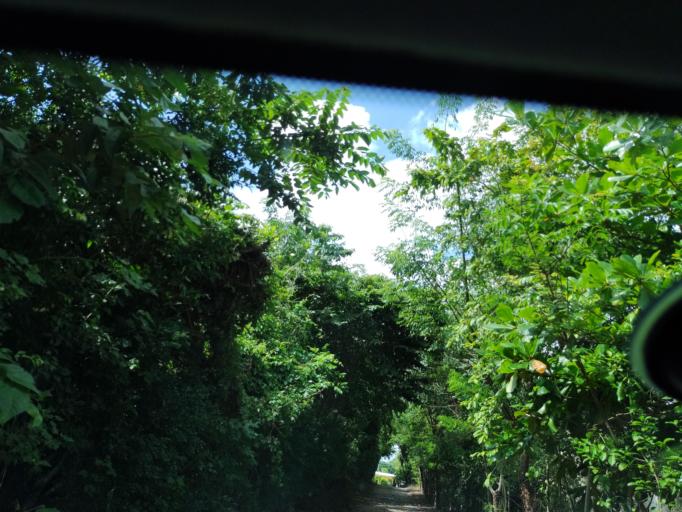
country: MX
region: Veracruz
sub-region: Martinez de la Torre
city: El Progreso
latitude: 20.1131
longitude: -97.0080
